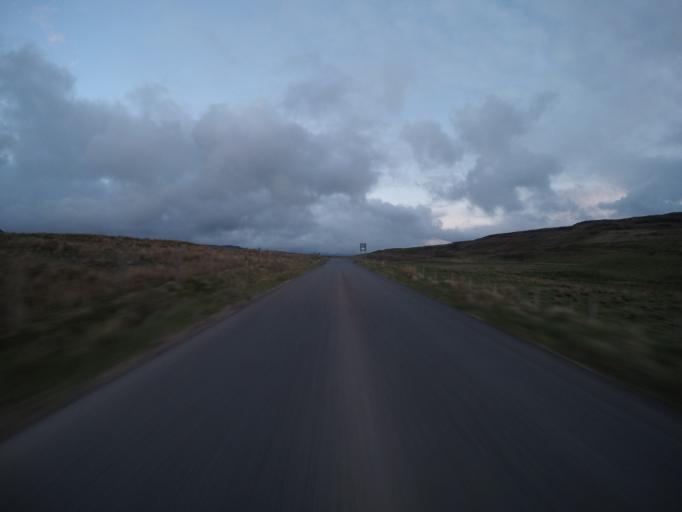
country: GB
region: Scotland
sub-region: Highland
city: Portree
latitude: 57.5984
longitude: -6.3758
